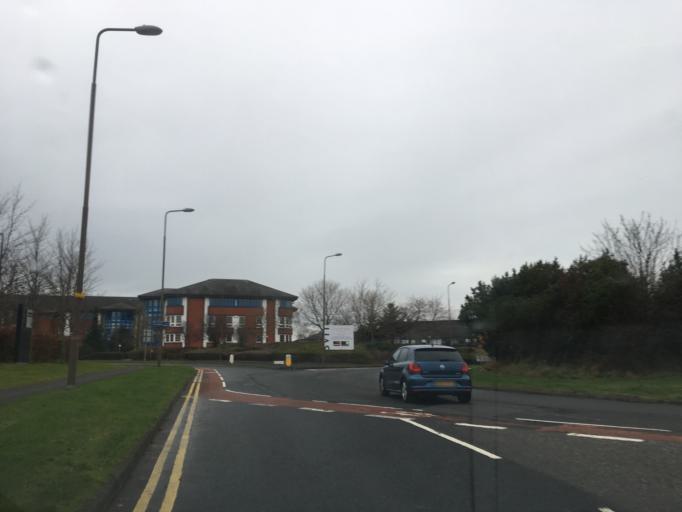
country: GB
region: Scotland
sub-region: Edinburgh
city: Currie
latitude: 55.9346
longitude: -3.3065
